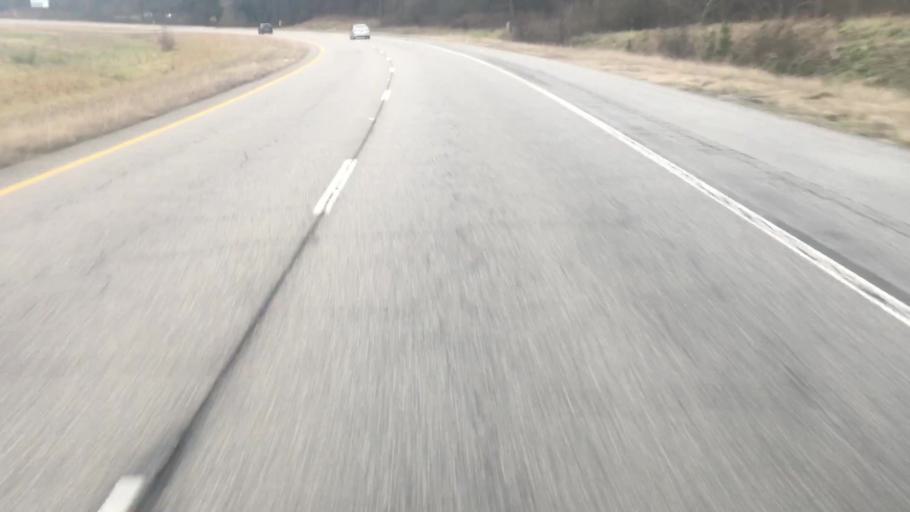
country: US
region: Alabama
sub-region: Walker County
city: Cordova
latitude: 33.8099
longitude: -87.1472
